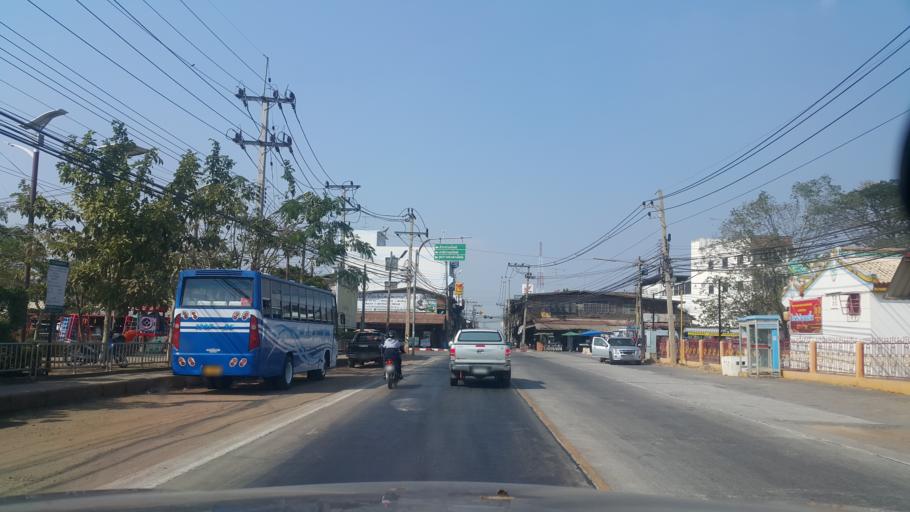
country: TH
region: Nakhon Ratchasima
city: Chok Chai
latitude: 14.7316
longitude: 102.1658
